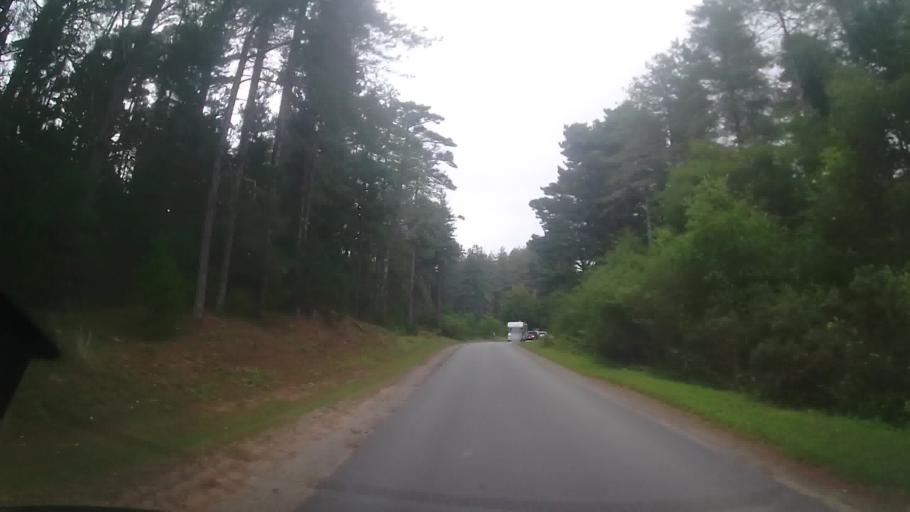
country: GB
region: Wales
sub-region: Gwynedd
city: Caernarfon
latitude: 53.1490
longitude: -4.3826
